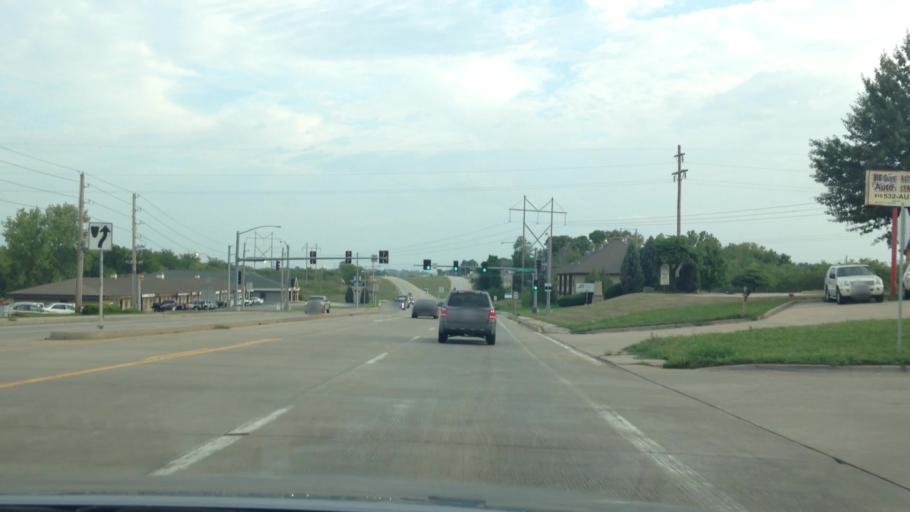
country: US
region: Missouri
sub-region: Clay County
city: Smithville
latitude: 39.3625
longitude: -94.5838
